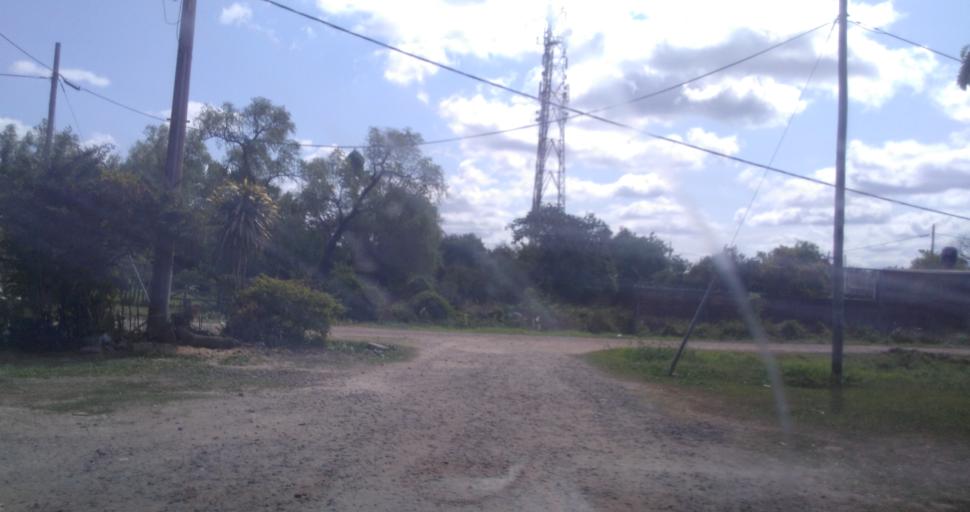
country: AR
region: Chaco
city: Fontana
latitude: -27.4269
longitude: -59.0308
